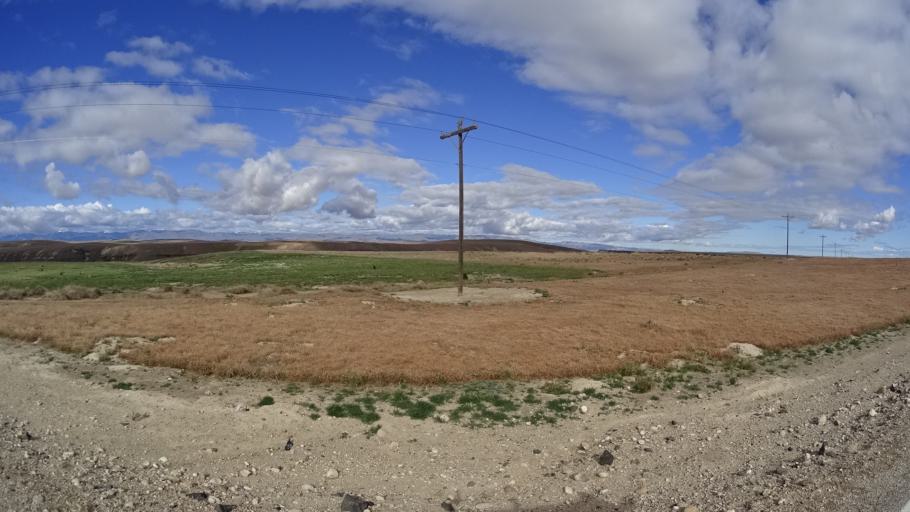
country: US
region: Idaho
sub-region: Owyhee County
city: Murphy
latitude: 43.2774
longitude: -116.3942
